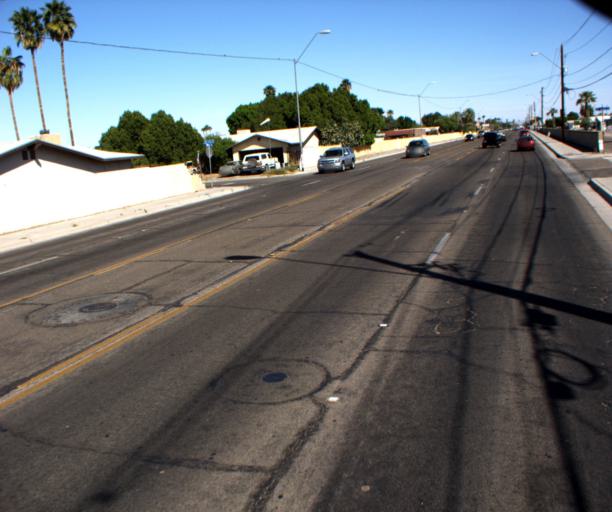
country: US
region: Arizona
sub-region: Yuma County
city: Yuma
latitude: 32.6875
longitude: -114.6503
